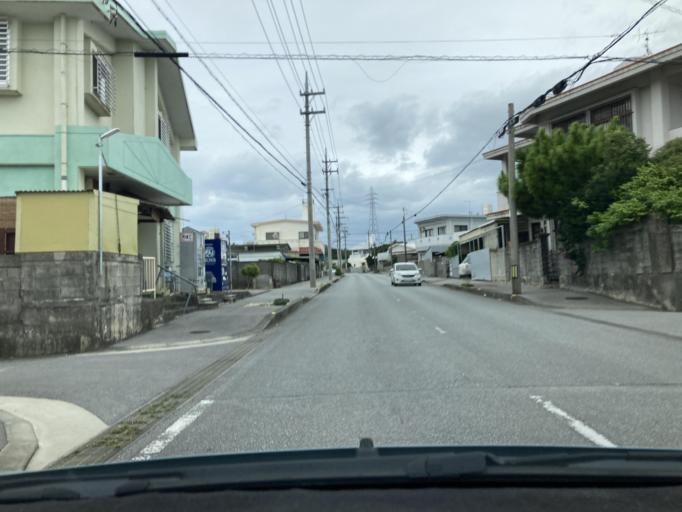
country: JP
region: Okinawa
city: Itoman
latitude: 26.1435
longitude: 127.6865
